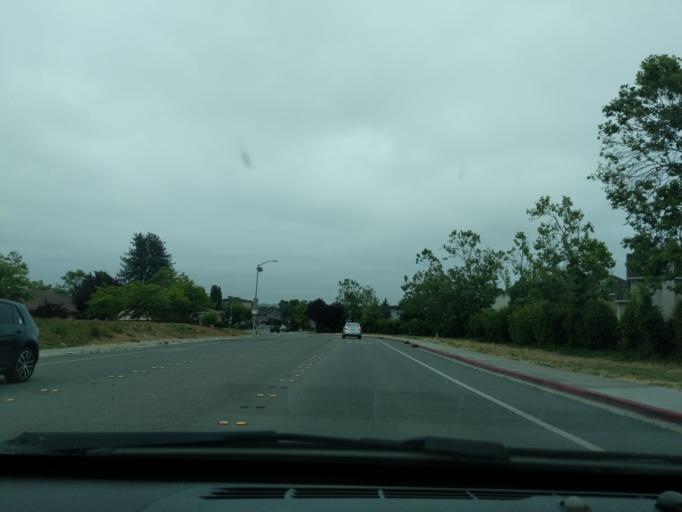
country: US
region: California
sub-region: Santa Cruz County
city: Freedom
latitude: 36.9216
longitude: -121.7739
